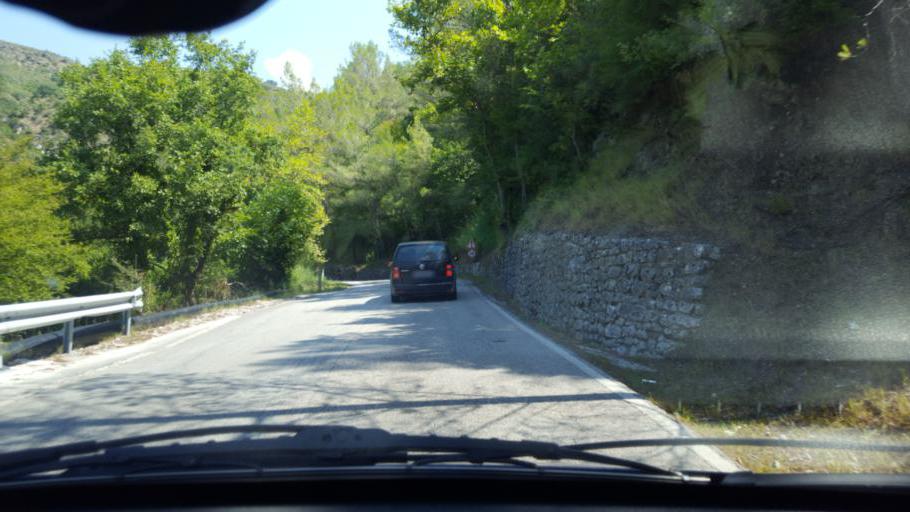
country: AL
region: Vlore
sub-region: Rrethi i Delvines
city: Mesopotam
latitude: 39.9212
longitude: 20.1611
